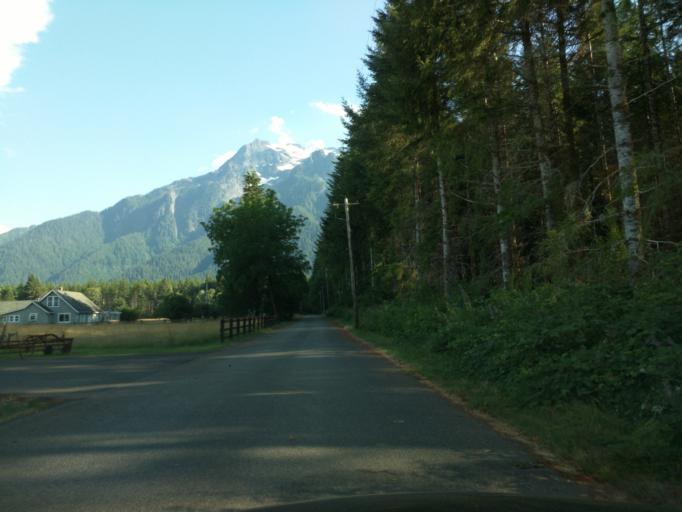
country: US
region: Washington
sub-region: Snohomish County
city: Darrington
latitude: 48.2652
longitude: -121.6815
